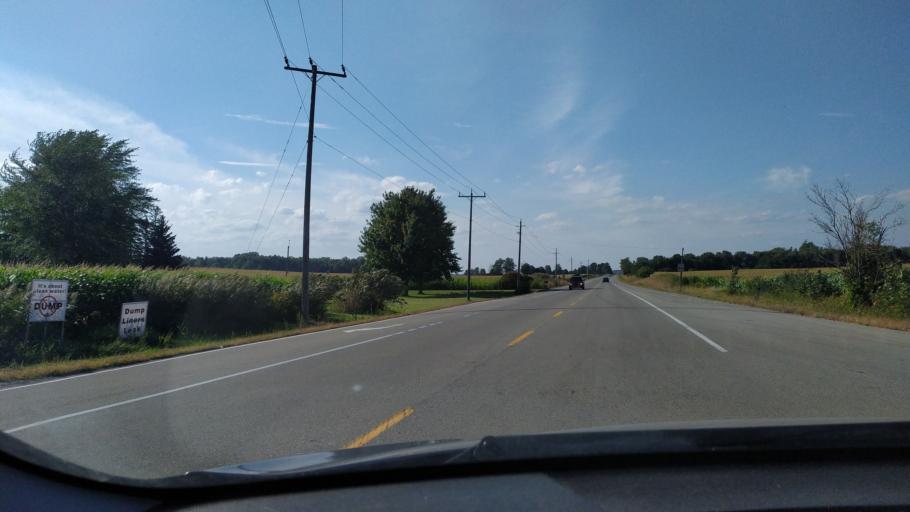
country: CA
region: Ontario
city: Ingersoll
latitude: 43.0549
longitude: -80.8272
